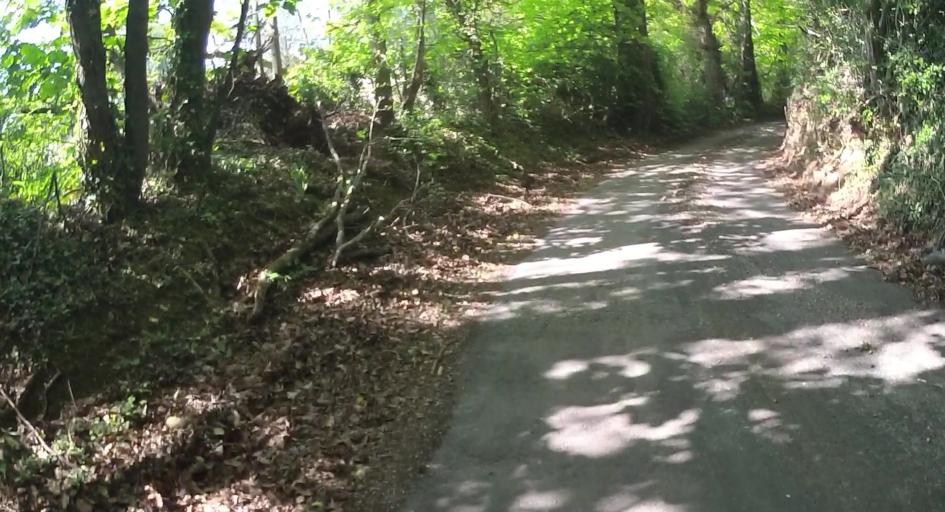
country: GB
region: England
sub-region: Hampshire
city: Alton
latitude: 51.1515
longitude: -1.0220
